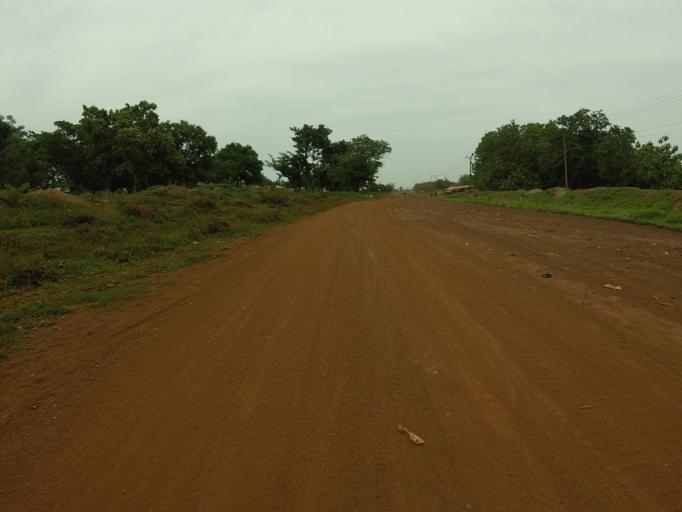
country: GH
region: Northern
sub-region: Yendi
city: Yendi
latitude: 9.2211
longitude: 0.0211
